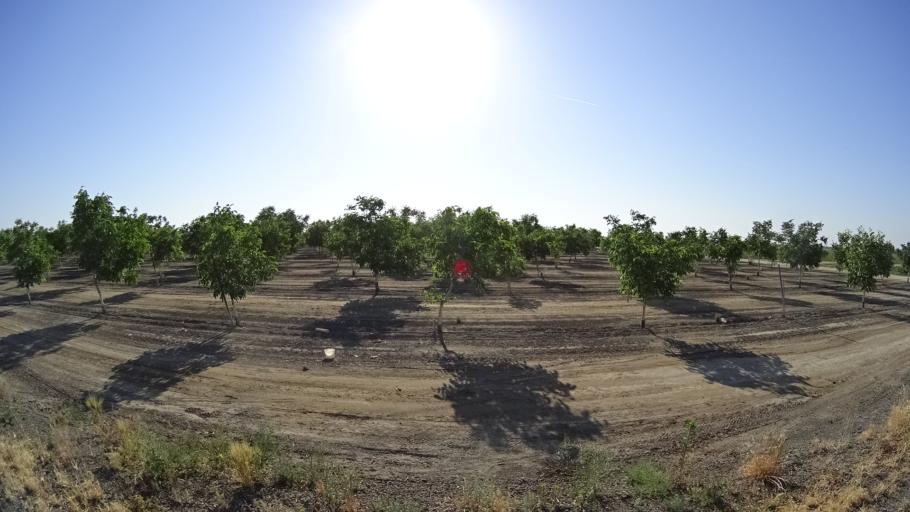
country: US
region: California
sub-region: Kings County
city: Armona
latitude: 36.2916
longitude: -119.7092
